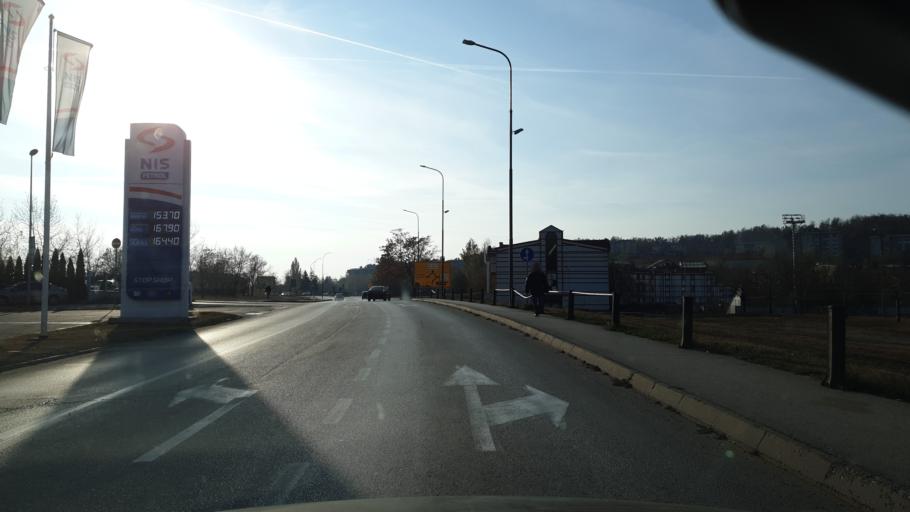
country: RS
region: Central Serbia
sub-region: Borski Okrug
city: Bor
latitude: 44.0575
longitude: 22.1056
